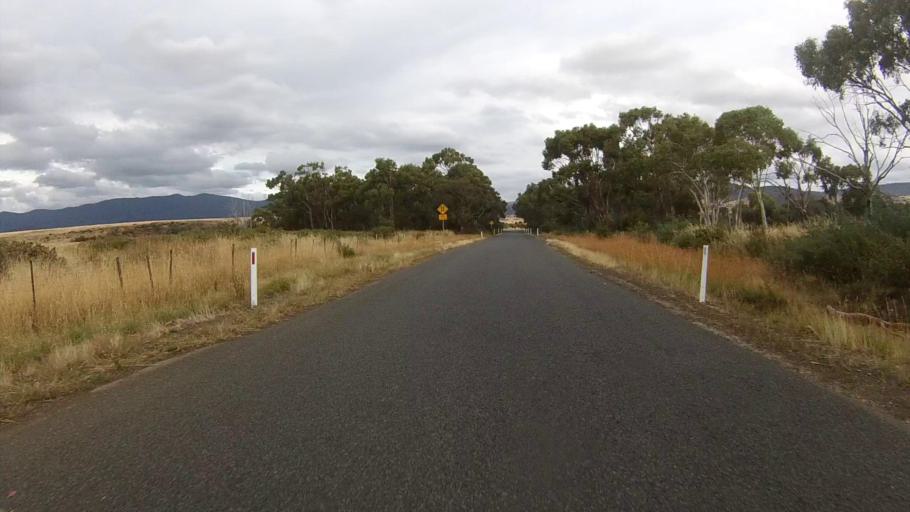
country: AU
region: Tasmania
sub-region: Northern Midlands
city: Evandale
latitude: -41.8135
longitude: 147.7539
